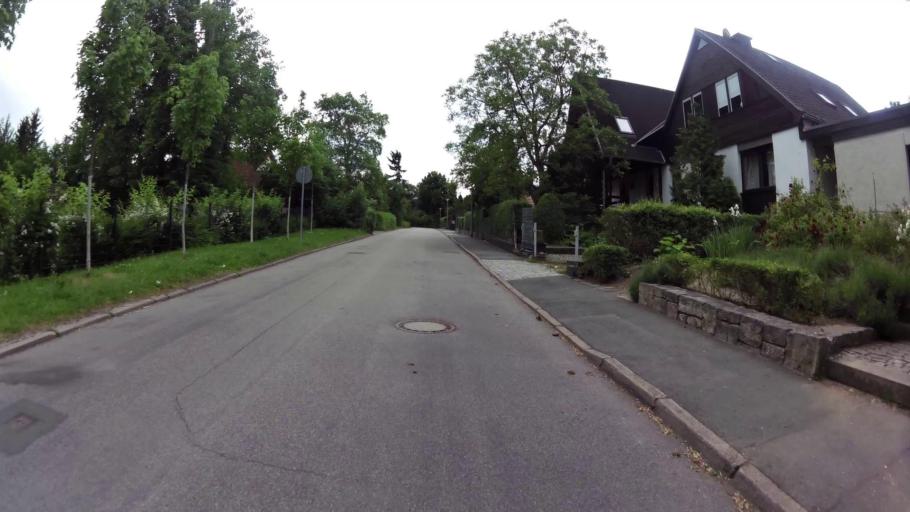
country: DE
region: Thuringia
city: Weimar
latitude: 50.9739
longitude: 11.3083
